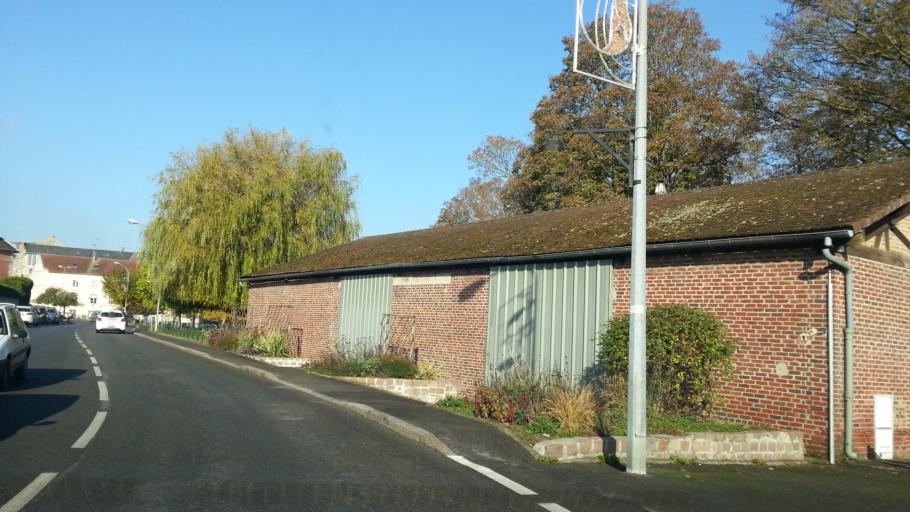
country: FR
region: Picardie
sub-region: Departement de l'Oise
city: Mouy
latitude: 49.3194
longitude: 2.3231
